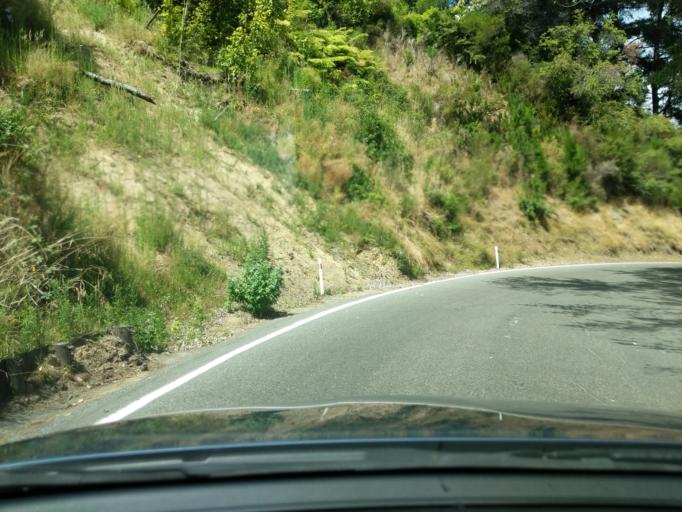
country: NZ
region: Tasman
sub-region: Tasman District
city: Motueka
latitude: -41.0519
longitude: 172.9624
